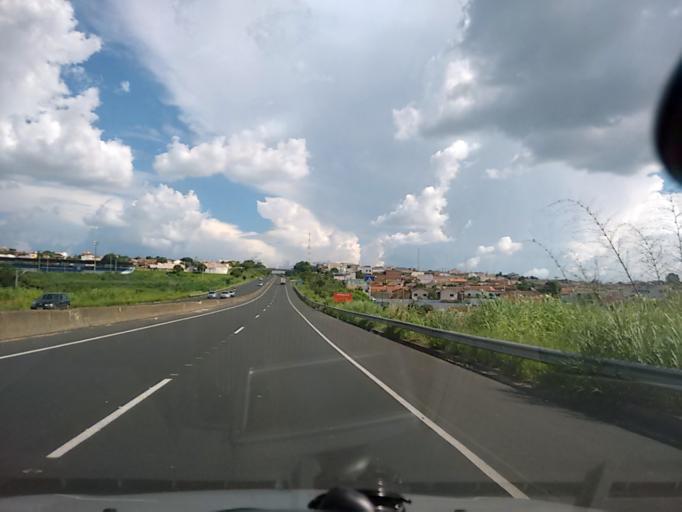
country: BR
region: Sao Paulo
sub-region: Marilia
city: Marilia
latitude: -22.1987
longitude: -49.9651
